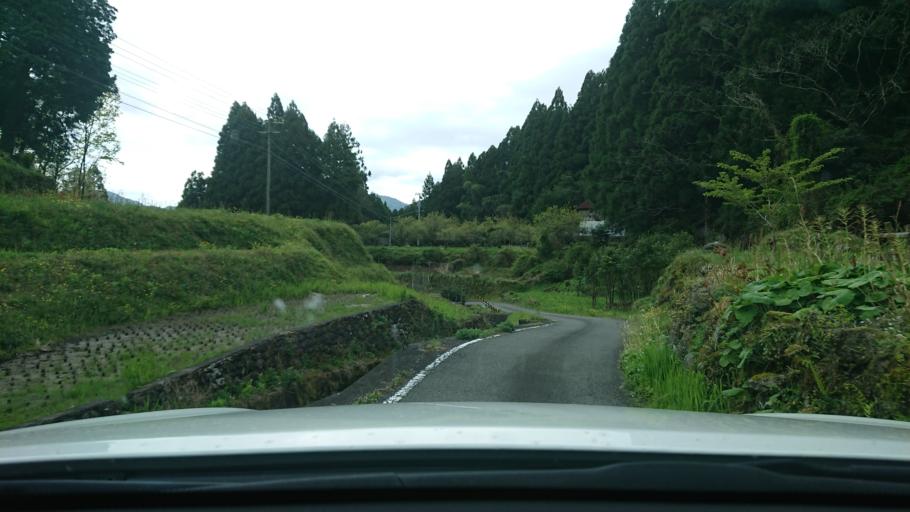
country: JP
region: Tokushima
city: Kamojimacho-jogejima
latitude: 33.8872
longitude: 134.3858
